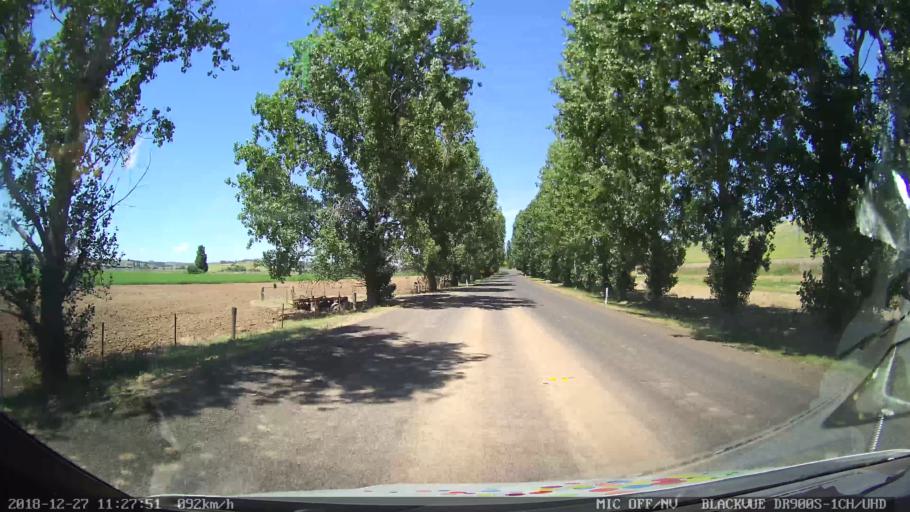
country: AU
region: New South Wales
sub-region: Bathurst Regional
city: Perthville
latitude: -33.4699
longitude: 149.5674
